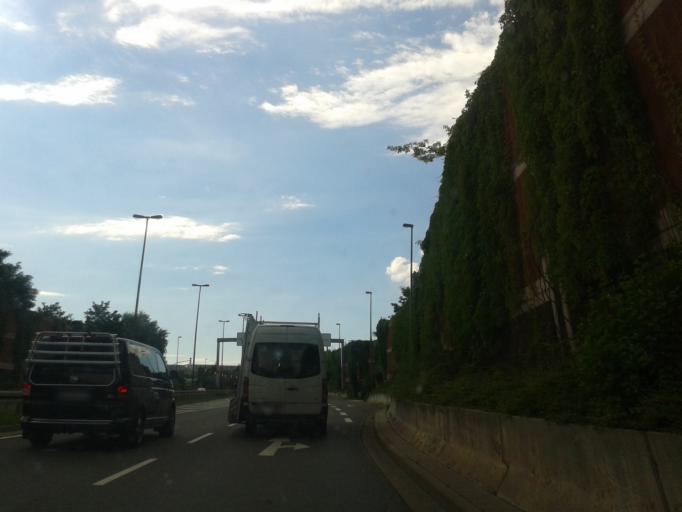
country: DE
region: Saxony
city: Dresden
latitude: 51.0482
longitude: 13.6835
